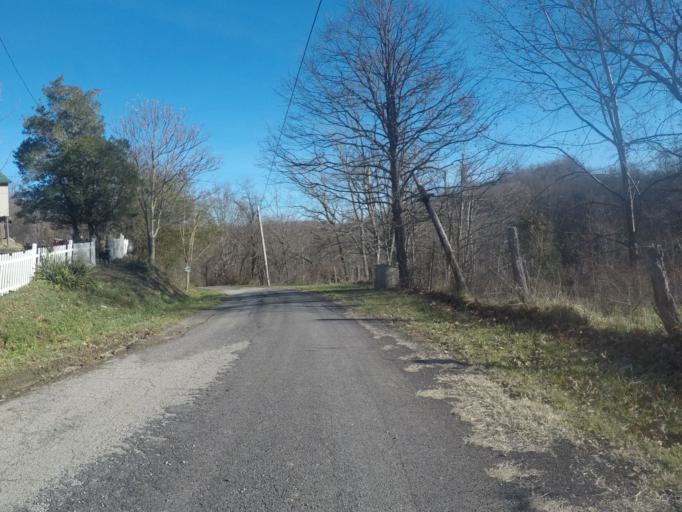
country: US
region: Ohio
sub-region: Lawrence County
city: Burlington
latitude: 38.3902
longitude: -82.4930
